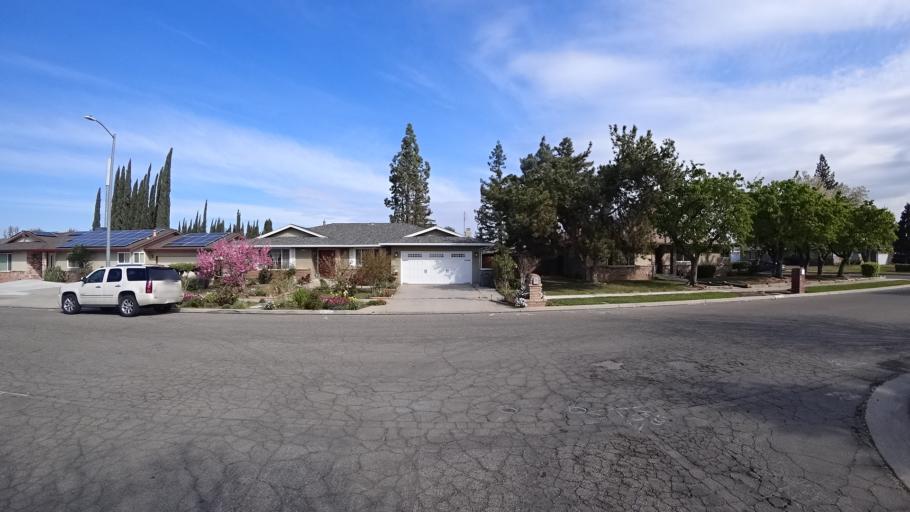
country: US
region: California
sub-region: Fresno County
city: Clovis
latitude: 36.8340
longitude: -119.7517
